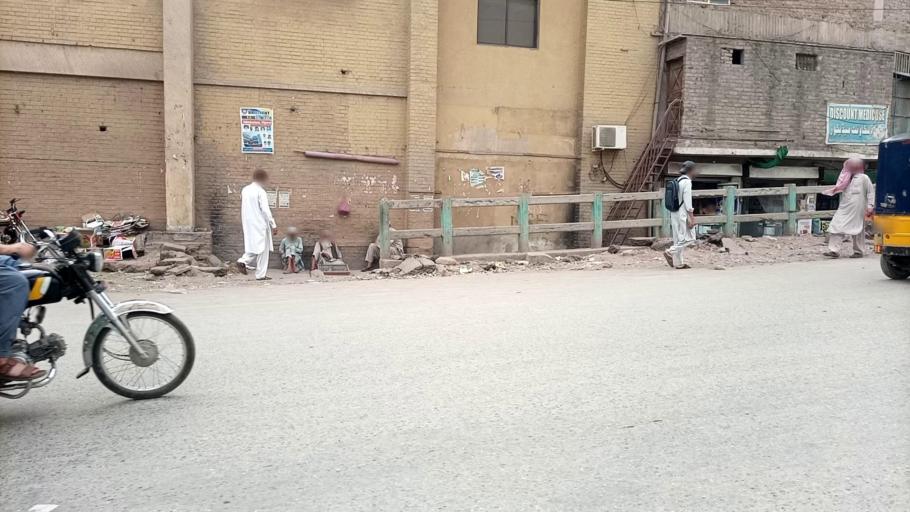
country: PK
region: Khyber Pakhtunkhwa
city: Peshawar
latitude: 34.0157
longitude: 71.5804
